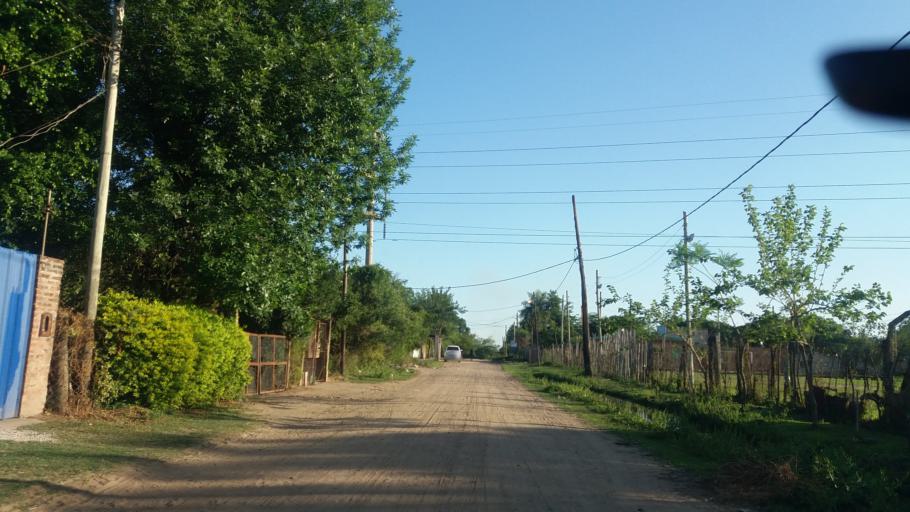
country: AR
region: Corrientes
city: Corrientes
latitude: -27.5135
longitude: -58.8320
